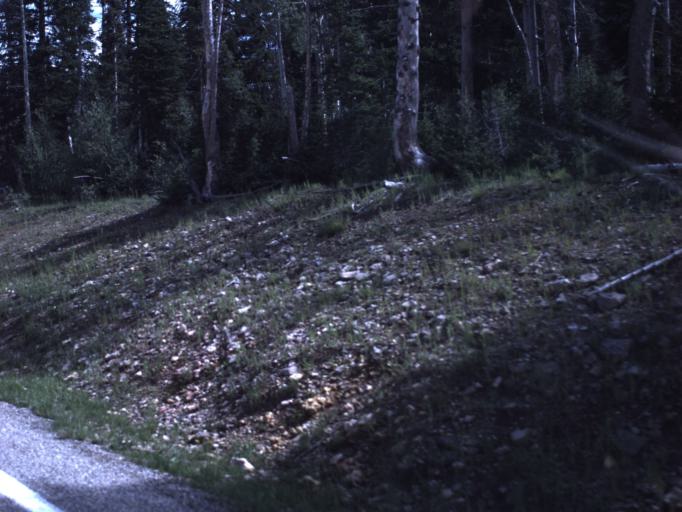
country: US
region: Utah
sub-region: Iron County
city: Cedar City
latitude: 37.5860
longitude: -112.8474
